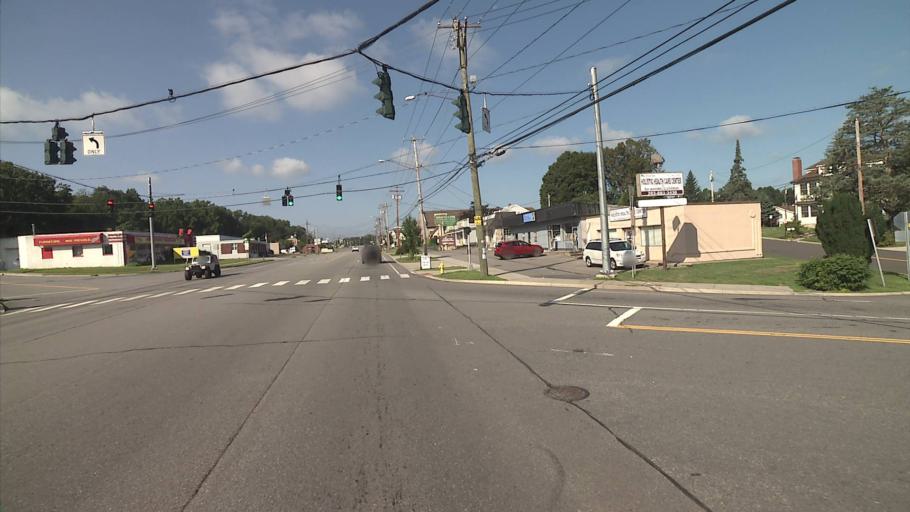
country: US
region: Connecticut
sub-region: New Haven County
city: City of Milford (balance)
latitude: 41.2308
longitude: -73.0640
